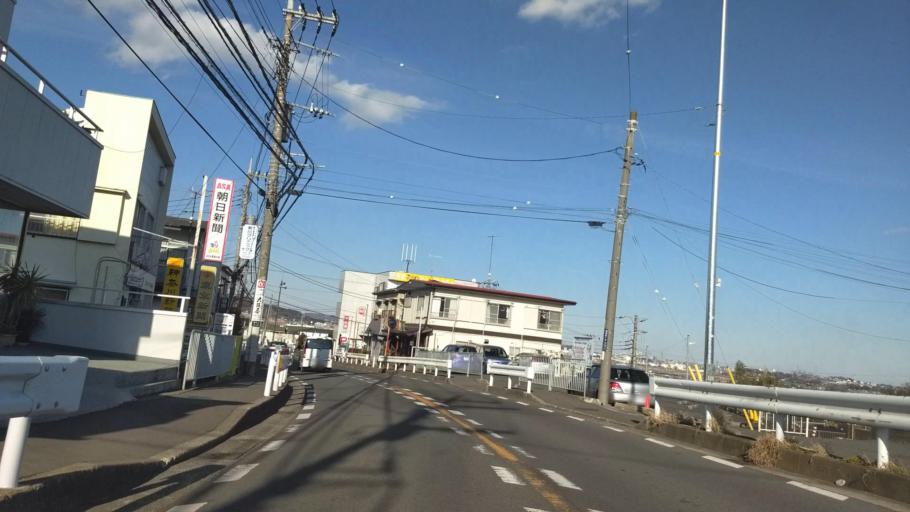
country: JP
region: Kanagawa
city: Isehara
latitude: 35.3681
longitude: 139.2738
